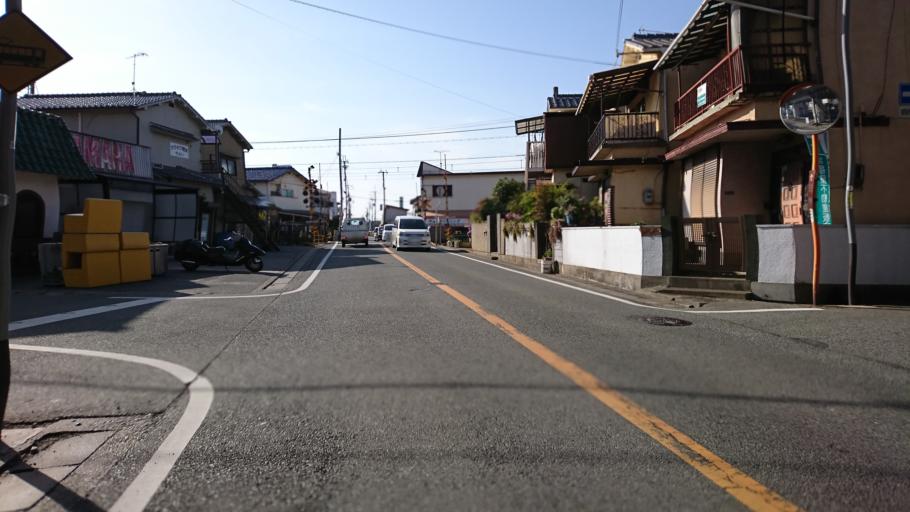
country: JP
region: Hyogo
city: Kakogawacho-honmachi
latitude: 34.7221
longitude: 134.8638
